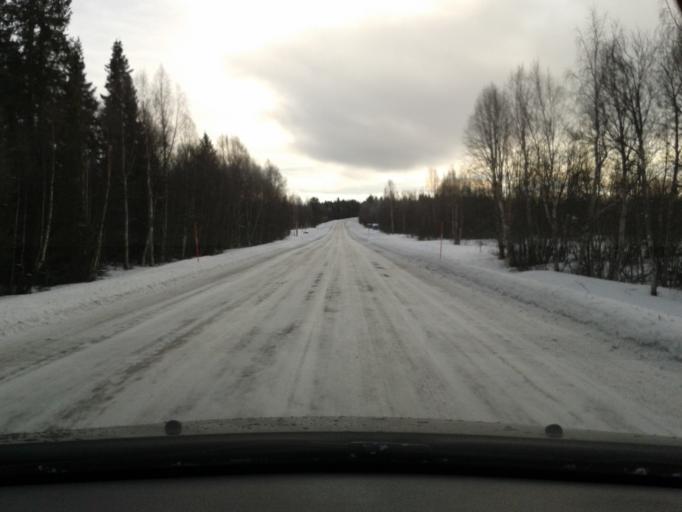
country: SE
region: Vaesterbotten
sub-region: Vilhelmina Kommun
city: Sjoberg
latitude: 64.7653
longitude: 16.1515
